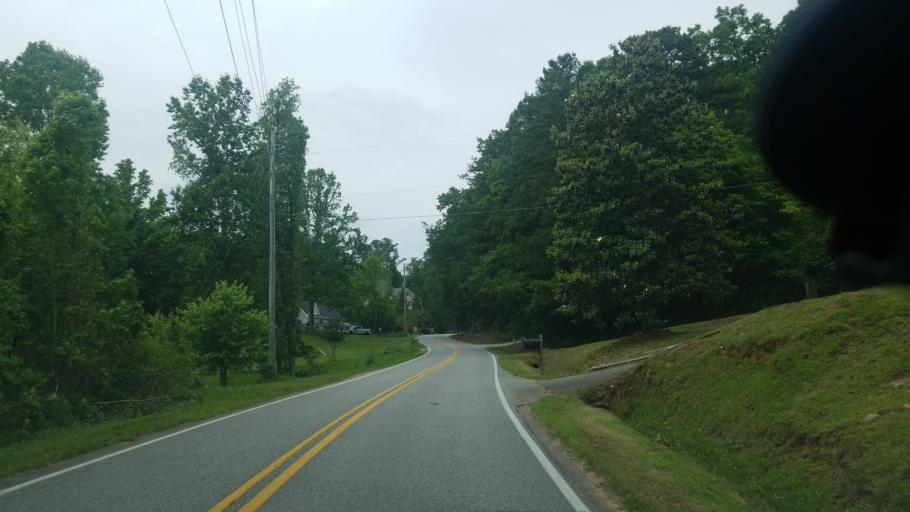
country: US
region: Georgia
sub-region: Forsyth County
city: Cumming
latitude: 34.1512
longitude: -84.1301
